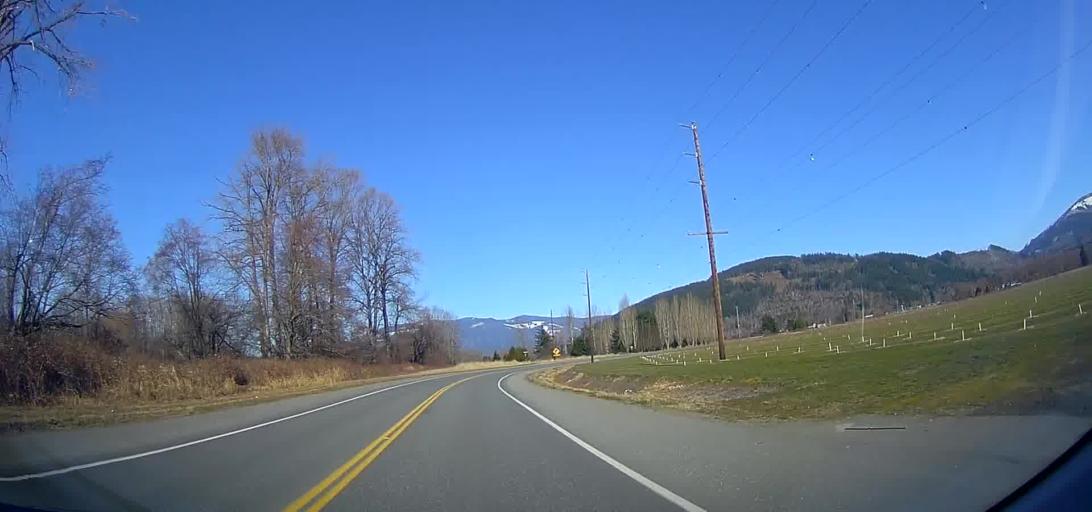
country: US
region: Washington
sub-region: Skagit County
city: Clear Lake
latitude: 48.4663
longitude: -122.2562
